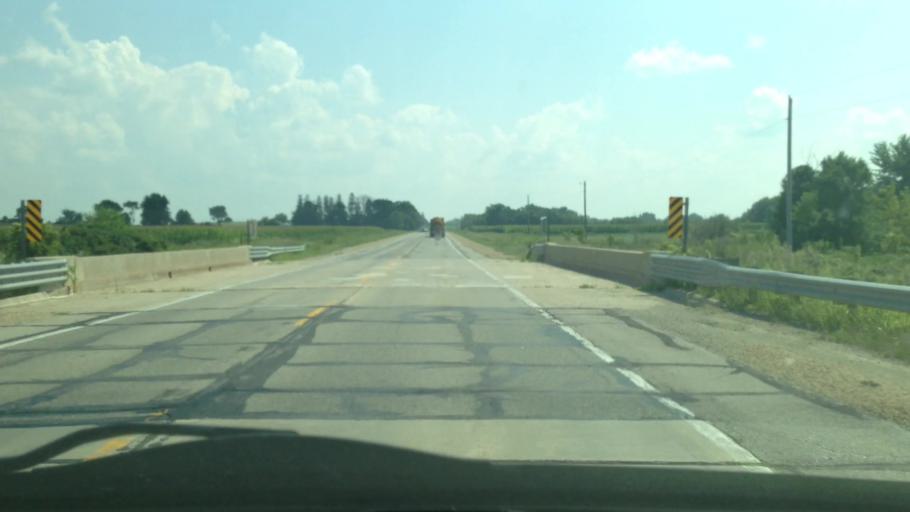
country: US
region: Iowa
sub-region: Chickasaw County
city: New Hampton
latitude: 43.2097
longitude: -92.2984
